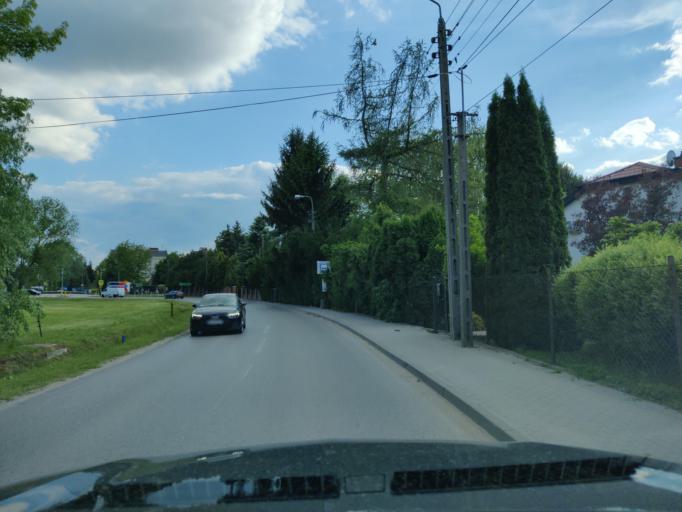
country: PL
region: Masovian Voivodeship
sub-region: Powiat piaseczynski
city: Konstancin-Jeziorna
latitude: 52.1029
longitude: 21.1258
